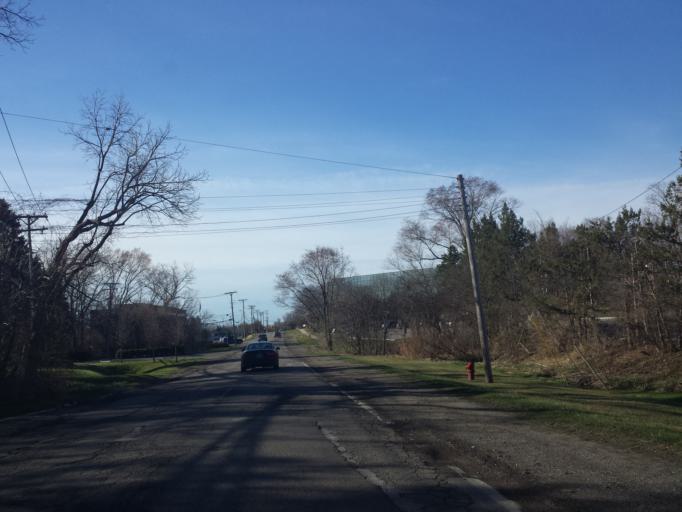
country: US
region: Michigan
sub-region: Oakland County
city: Franklin
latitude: 42.5051
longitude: -83.3100
